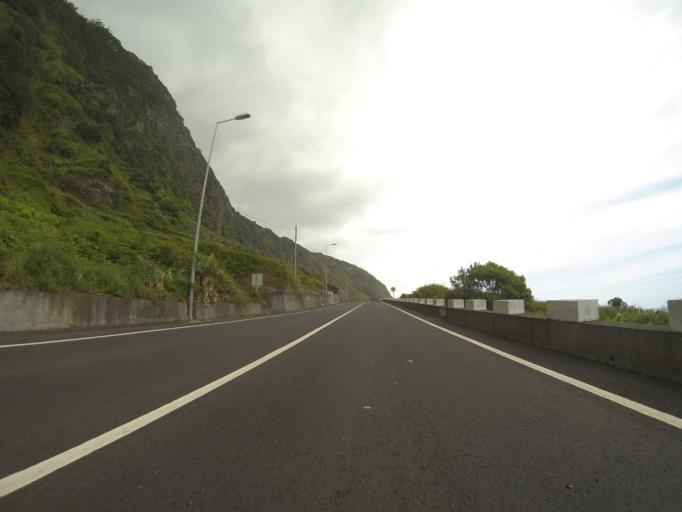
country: PT
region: Madeira
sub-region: Porto Moniz
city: Porto Moniz
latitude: 32.8456
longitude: -17.1469
